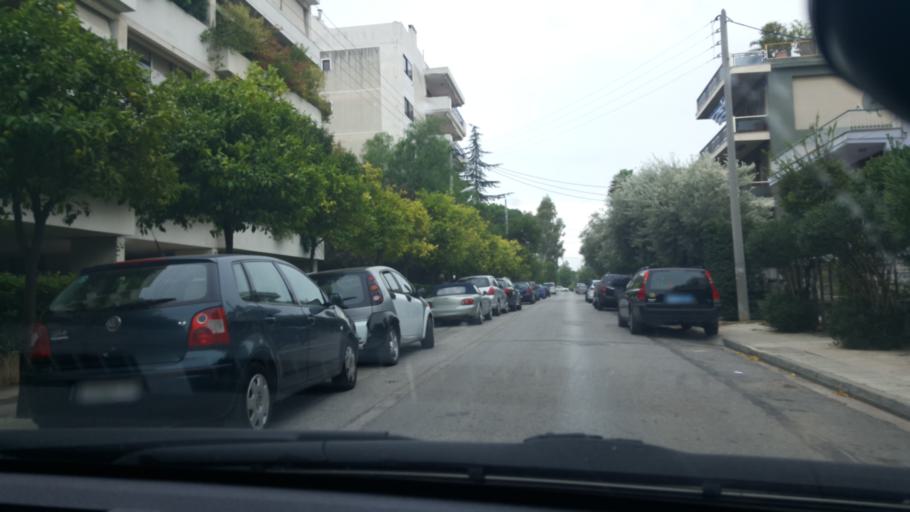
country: GR
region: Attica
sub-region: Nomarchia Athinas
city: Neo Psychiko
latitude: 38.0137
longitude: 23.7856
